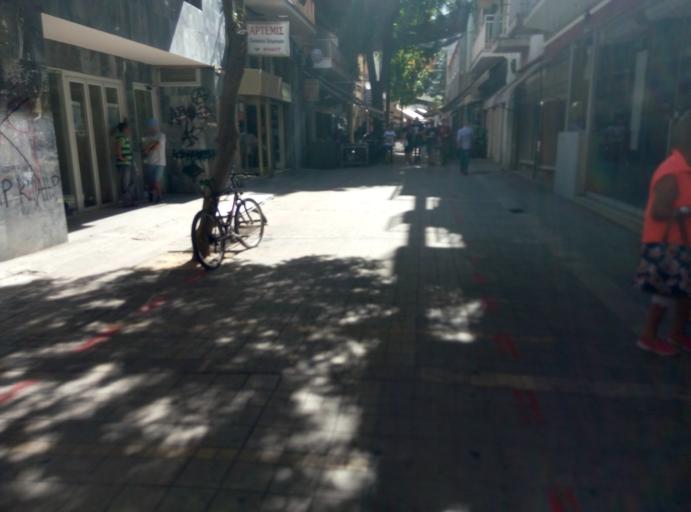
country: CY
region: Lefkosia
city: Nicosia
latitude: 35.1709
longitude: 33.3616
